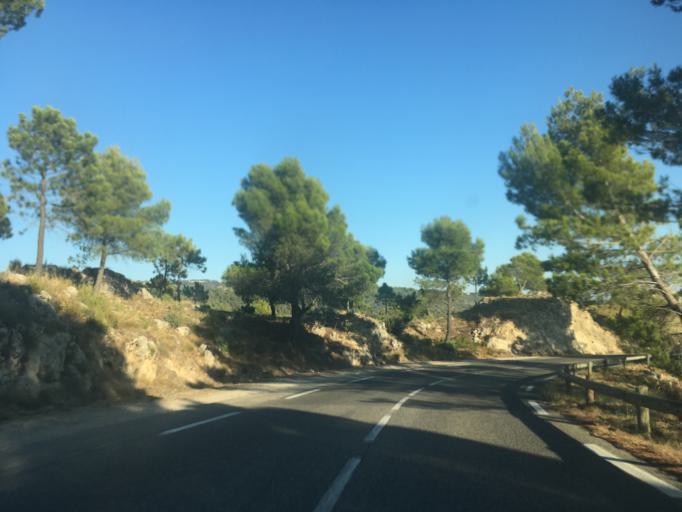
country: FR
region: Provence-Alpes-Cote d'Azur
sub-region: Departement du Var
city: Villecroze
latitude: 43.5860
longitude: 6.2634
